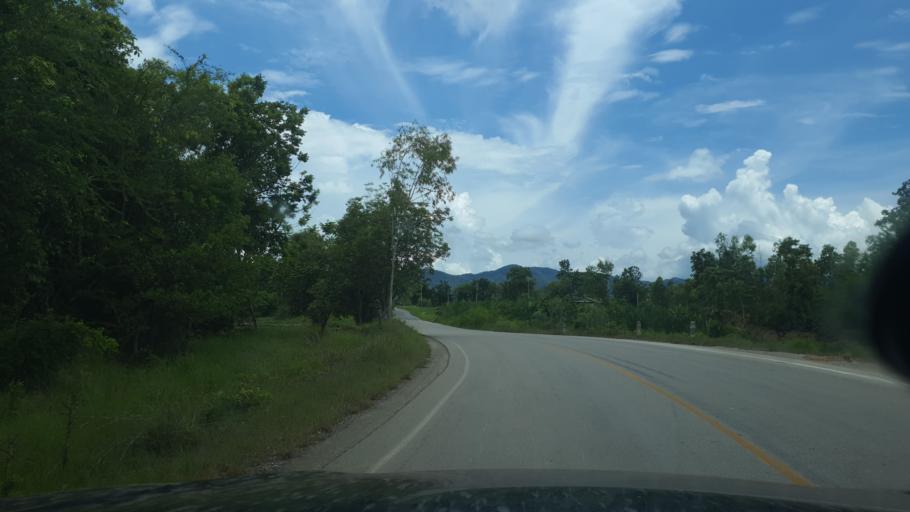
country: TH
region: Lampang
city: Sop Prap
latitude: 17.9155
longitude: 99.3882
